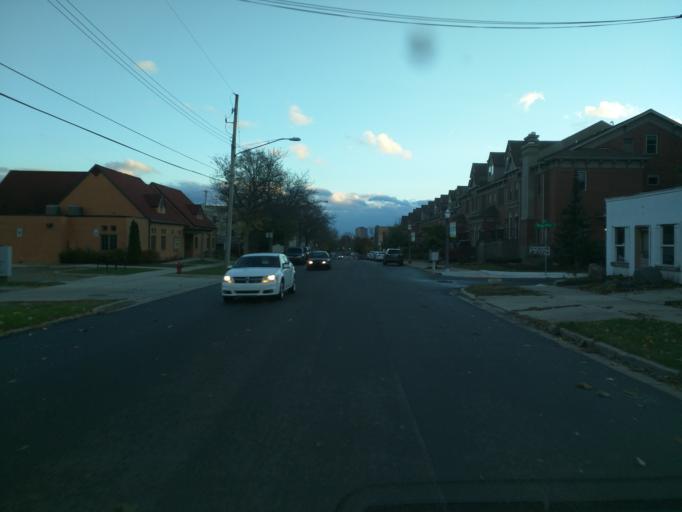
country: US
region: Michigan
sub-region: Ingham County
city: Lansing
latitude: 42.7502
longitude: -84.5496
